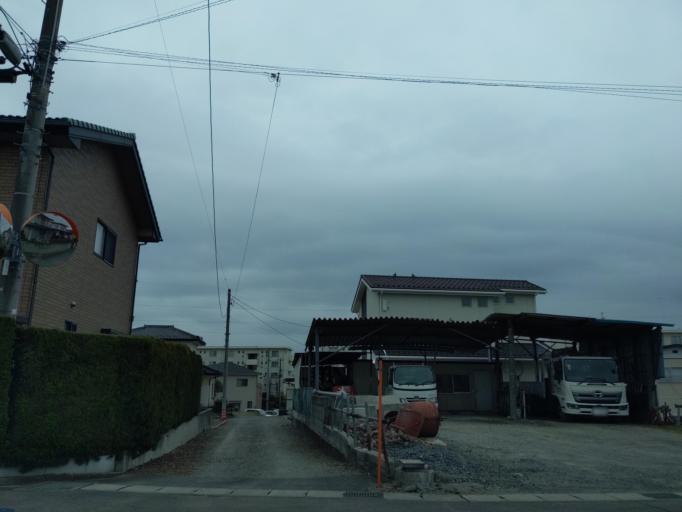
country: JP
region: Fukushima
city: Koriyama
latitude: 37.3783
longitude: 140.3412
